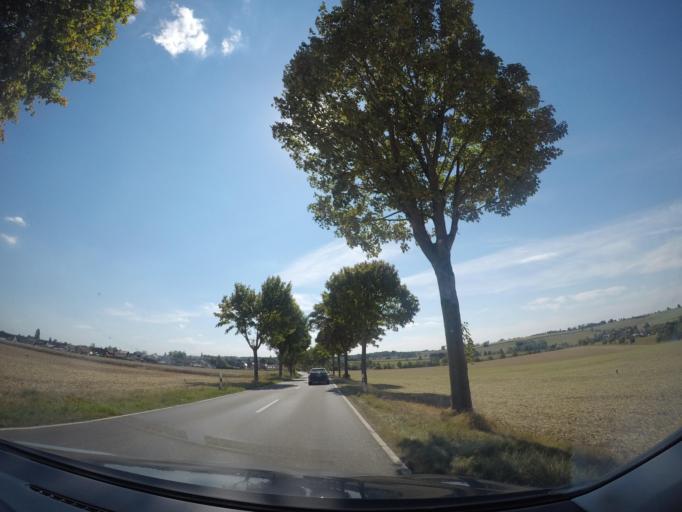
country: DE
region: Lower Saxony
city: Bad Lauterberg im Harz
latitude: 51.5975
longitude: 10.4756
